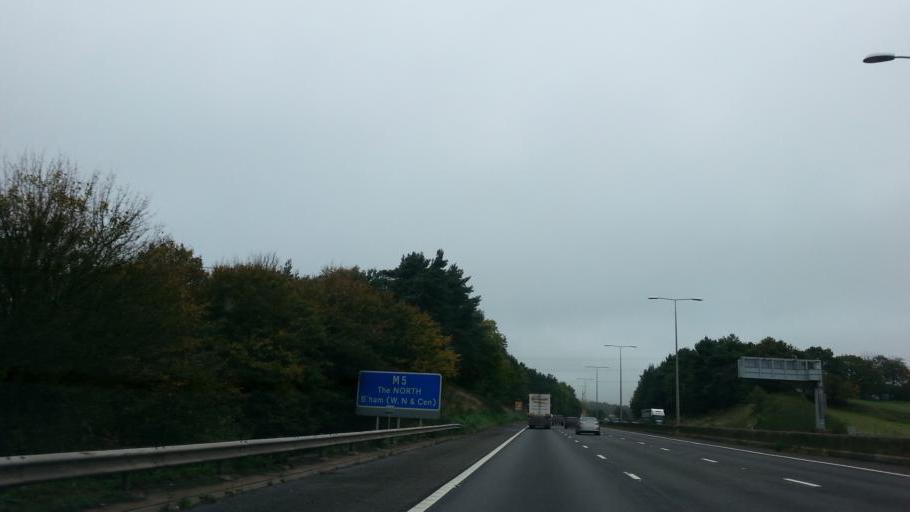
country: GB
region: England
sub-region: Worcestershire
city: Barnt Green
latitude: 52.3911
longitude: -2.0519
